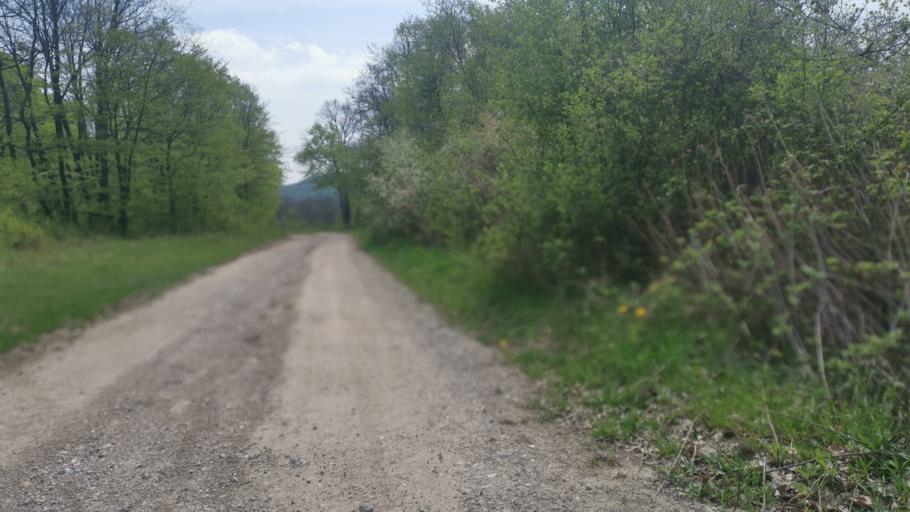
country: SK
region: Trnavsky
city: Smolenice
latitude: 48.5479
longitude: 17.4416
